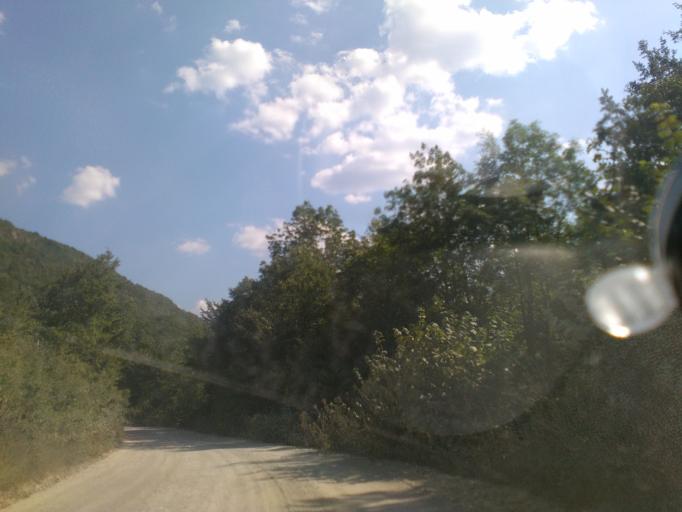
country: BA
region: Federation of Bosnia and Herzegovina
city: Orasac
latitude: 44.5180
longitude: 16.1249
